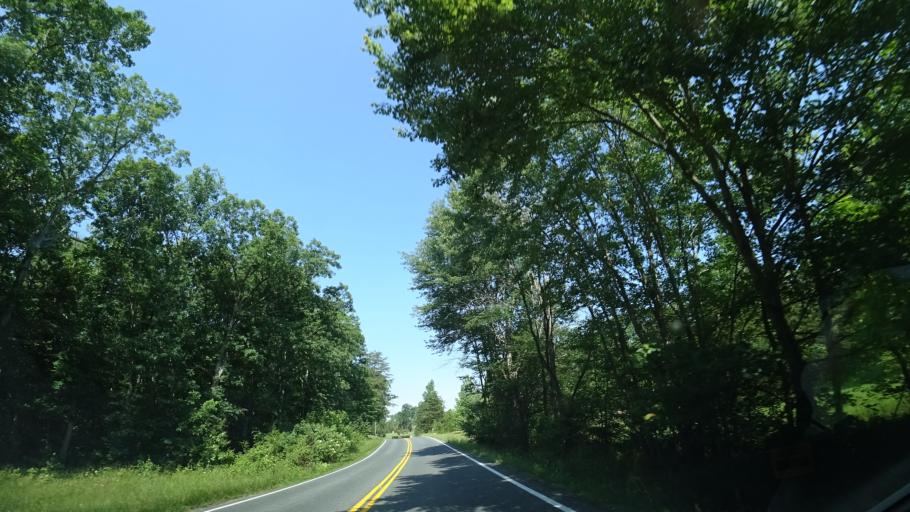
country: US
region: Virginia
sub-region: Louisa County
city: Louisa
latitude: 38.0840
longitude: -77.8420
